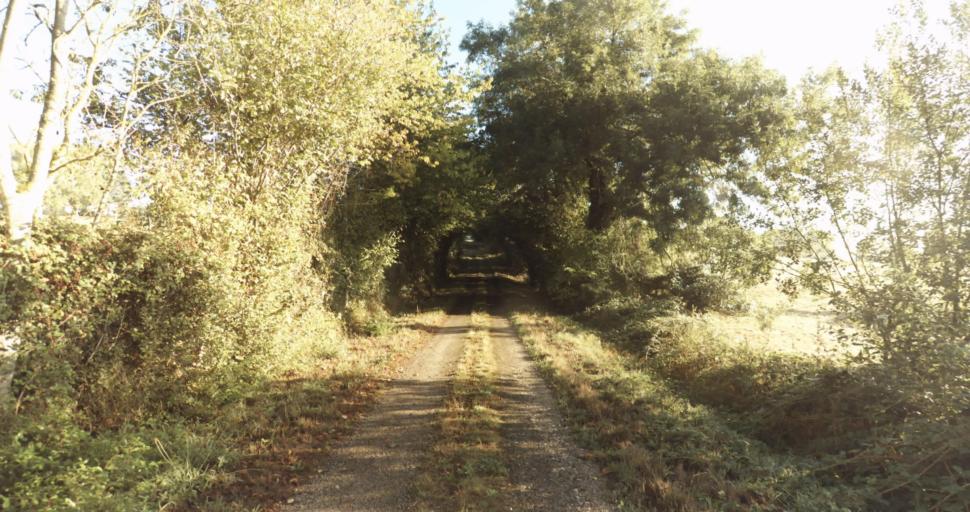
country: FR
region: Lower Normandy
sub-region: Departement de l'Orne
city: Vimoutiers
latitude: 48.9106
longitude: 0.1661
